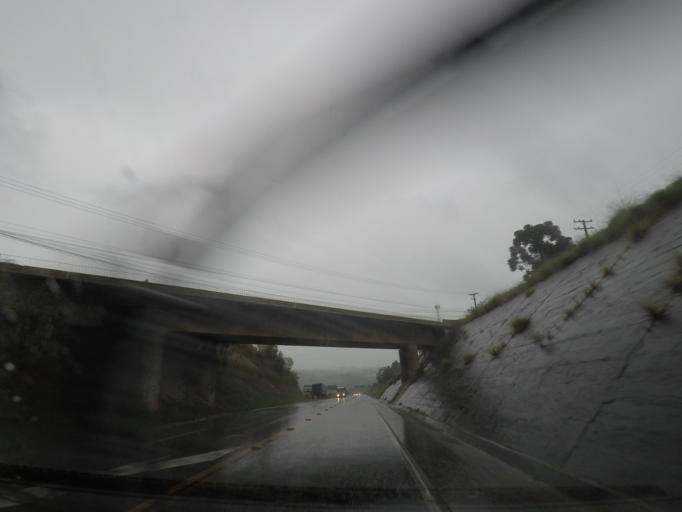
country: BR
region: Parana
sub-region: Almirante Tamandare
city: Almirante Tamandare
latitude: -25.3538
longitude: -49.2918
